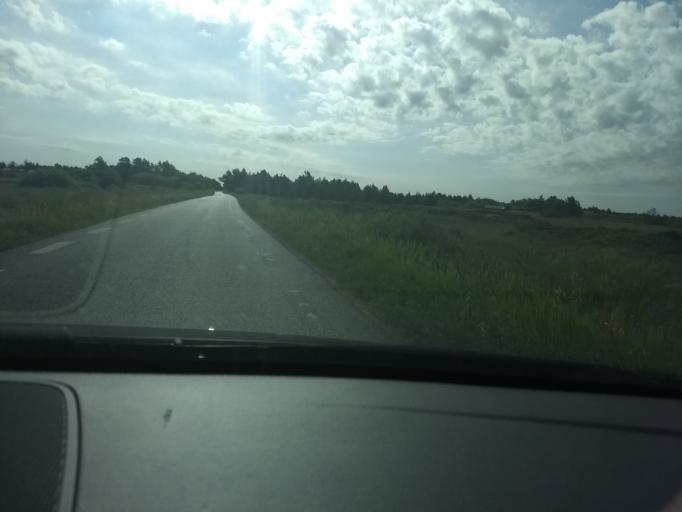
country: DE
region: Schleswig-Holstein
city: List
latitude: 55.1305
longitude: 8.5190
